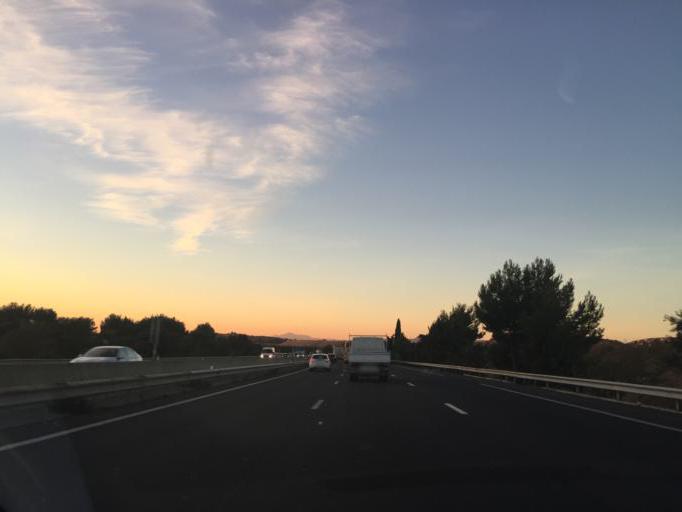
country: FR
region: Provence-Alpes-Cote d'Azur
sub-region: Departement des Bouches-du-Rhone
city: La Fare-les-Oliviers
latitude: 43.5843
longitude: 5.2049
